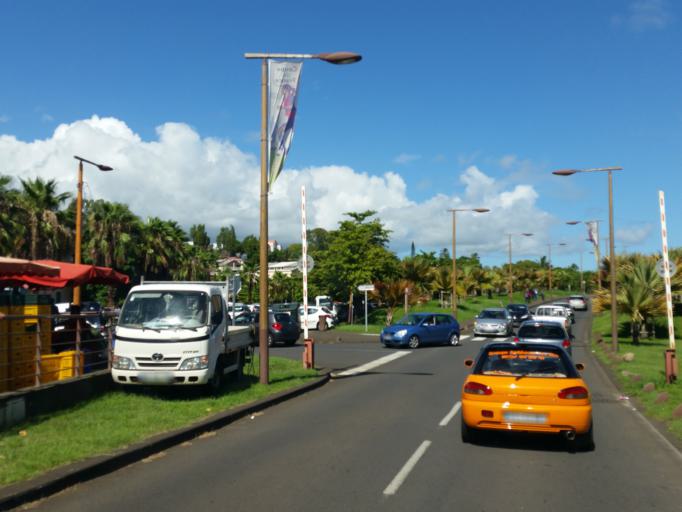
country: RE
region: Reunion
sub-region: Reunion
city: Sainte-Marie
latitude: -20.8961
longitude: 55.5491
